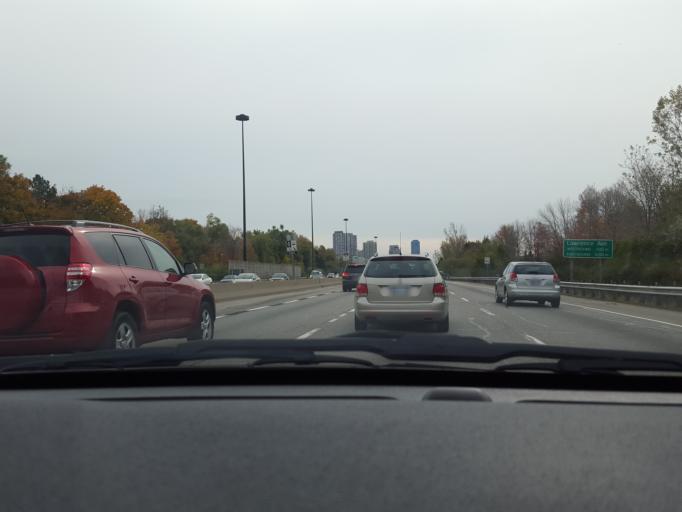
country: CA
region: Ontario
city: Willowdale
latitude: 43.7466
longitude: -79.3334
